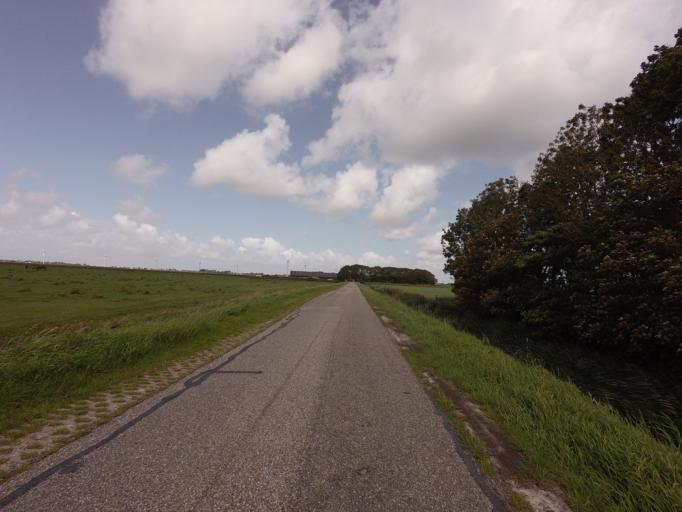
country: NL
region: Friesland
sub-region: Gemeente Franekeradeel
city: Sexbierum
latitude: 53.1705
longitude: 5.4887
